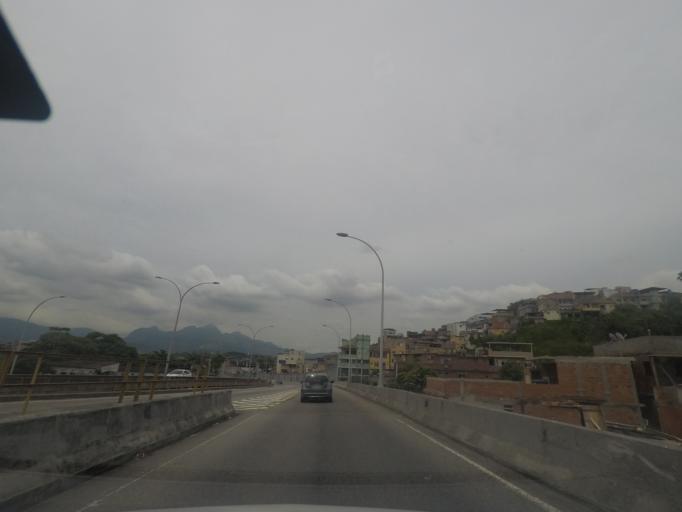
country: BR
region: Rio de Janeiro
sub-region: Rio De Janeiro
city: Rio de Janeiro
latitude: -22.8623
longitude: -43.2378
